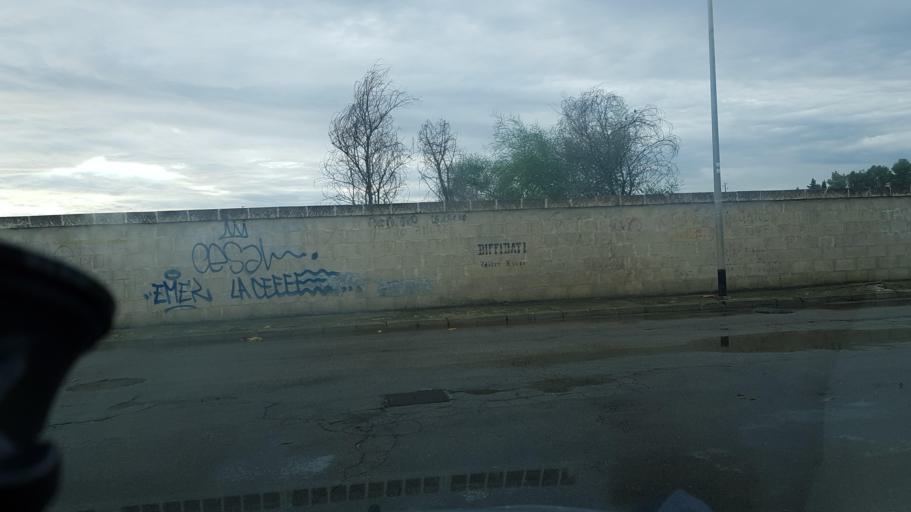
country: IT
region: Apulia
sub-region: Provincia di Lecce
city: Carmiano
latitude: 40.3497
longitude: 18.0366
